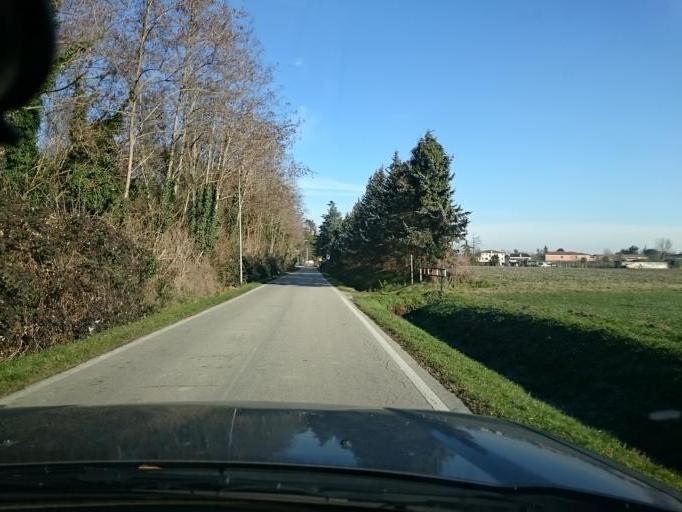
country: IT
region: Veneto
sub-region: Provincia di Padova
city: Saonara
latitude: 45.3701
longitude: 11.9774
